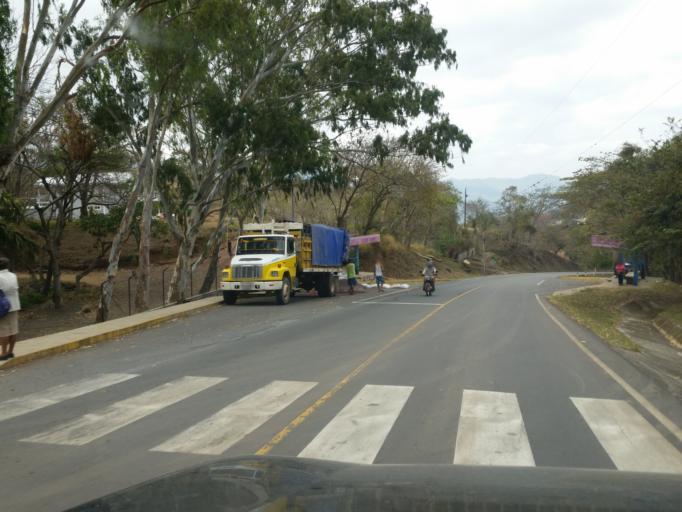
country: NI
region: Matagalpa
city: Matagalpa
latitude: 12.9589
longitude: -85.9196
